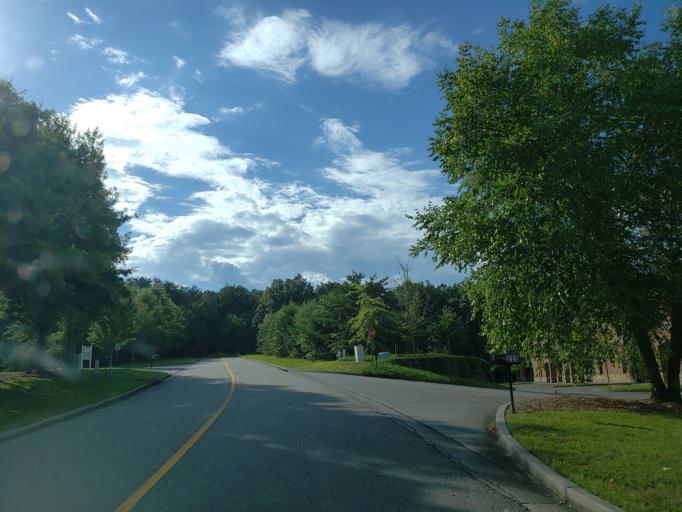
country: US
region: Georgia
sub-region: Cherokee County
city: Ball Ground
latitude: 34.3069
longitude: -84.4218
